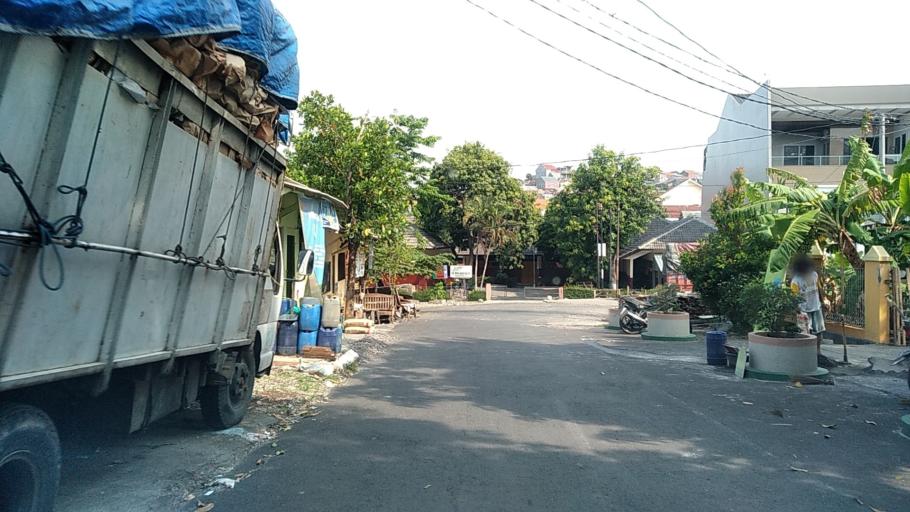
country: ID
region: Central Java
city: Semarang
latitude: -6.9926
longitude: 110.3838
